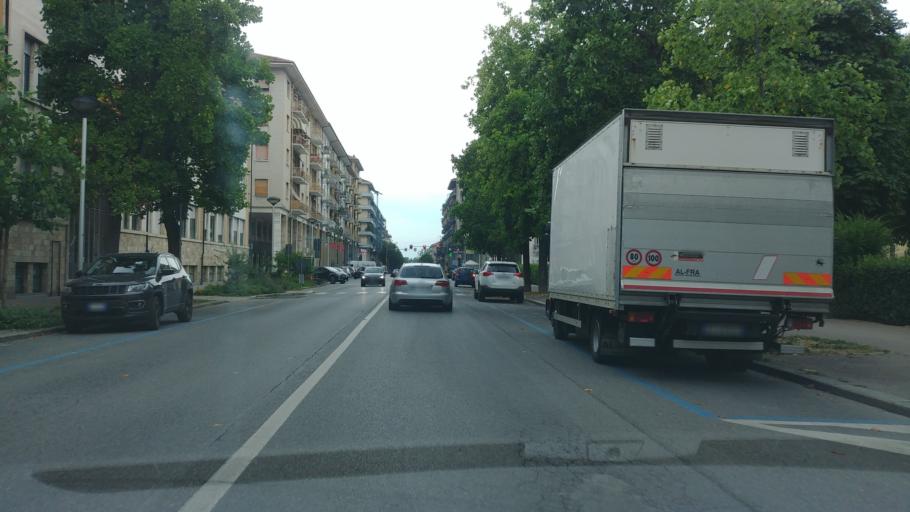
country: IT
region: Piedmont
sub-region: Provincia di Cuneo
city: Cuneo
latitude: 44.3824
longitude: 7.5373
